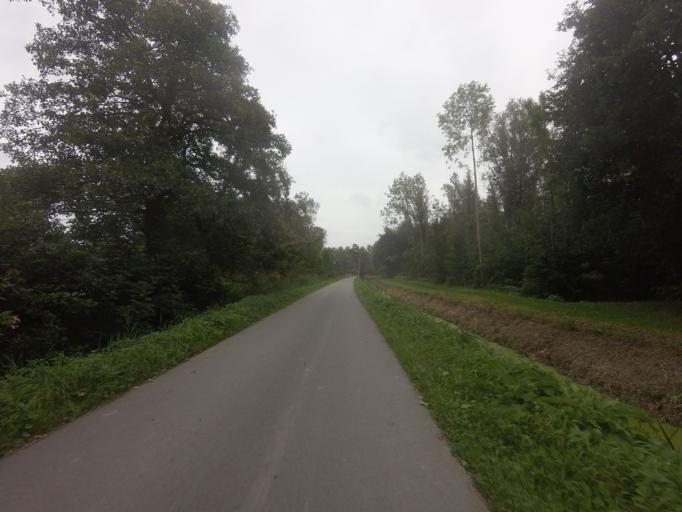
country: NL
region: Friesland
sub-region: Gemeente Leeuwarden
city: Bilgaard
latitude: 53.2223
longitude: 5.7898
